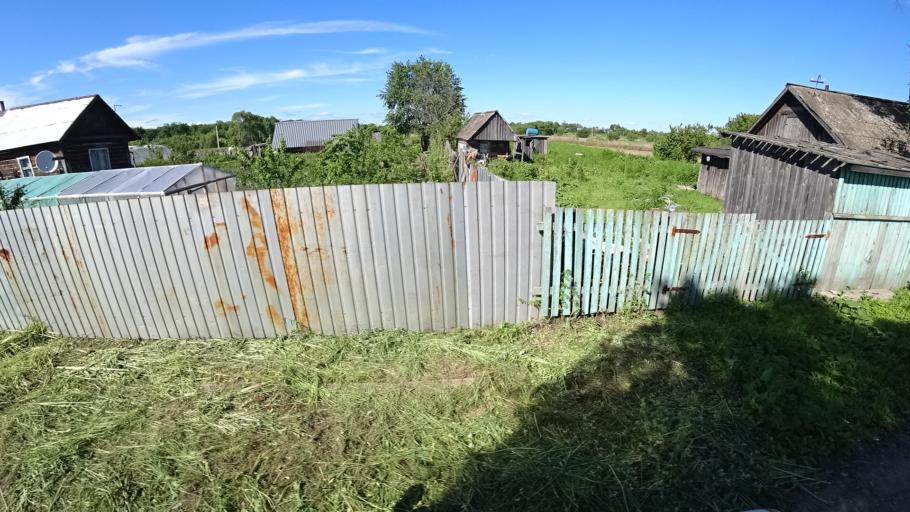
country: RU
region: Khabarovsk Krai
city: Khor
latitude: 47.8850
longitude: 135.0187
